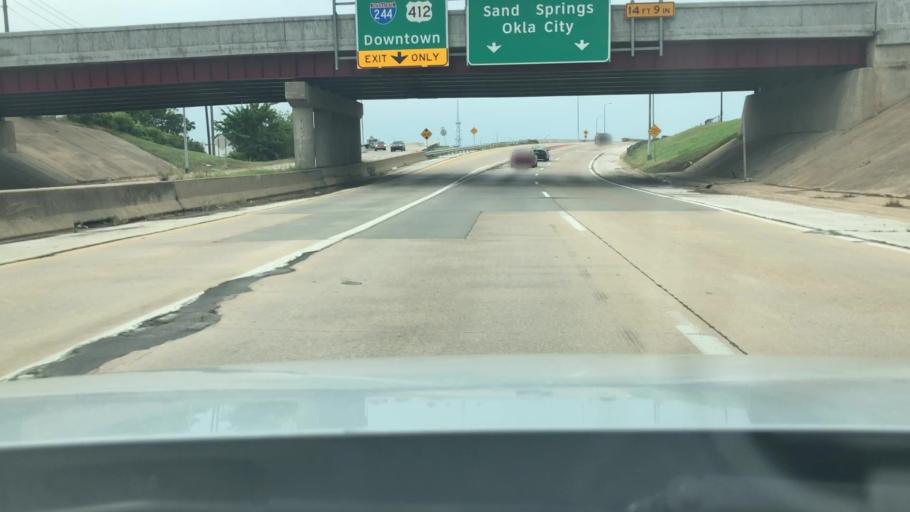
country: US
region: Oklahoma
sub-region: Tulsa County
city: Tulsa
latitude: 36.1628
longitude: -96.0008
